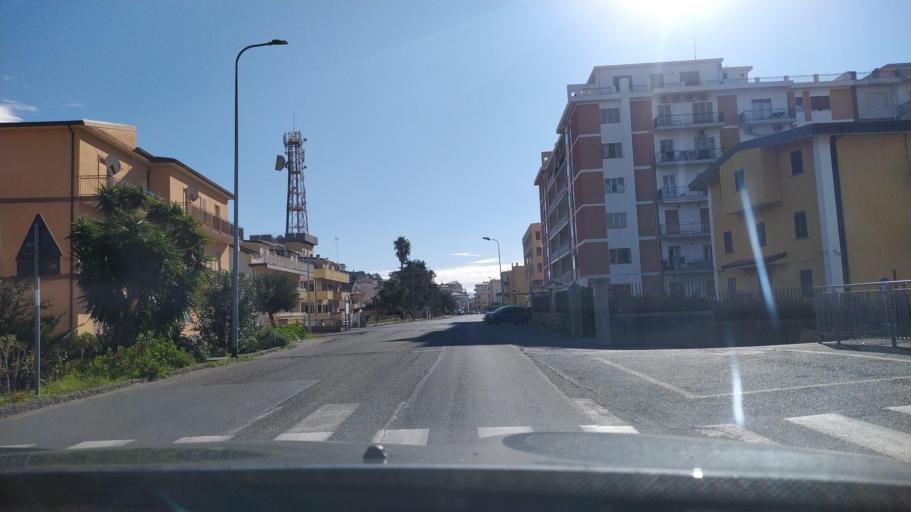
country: IT
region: Calabria
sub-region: Provincia di Cosenza
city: Paola
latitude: 39.3707
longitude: 16.0280
